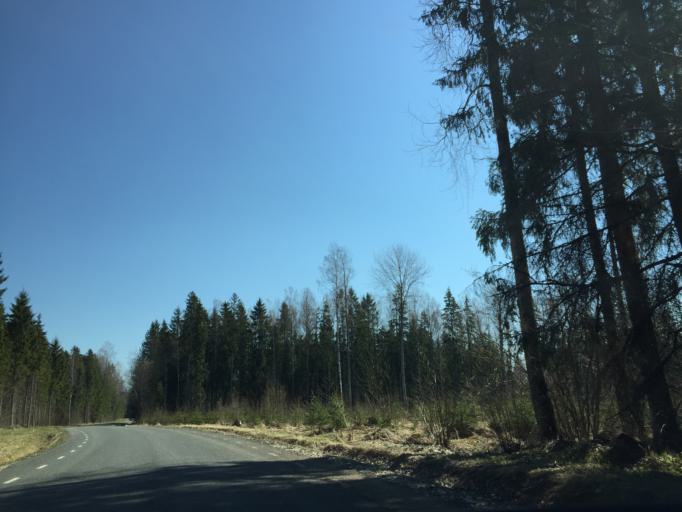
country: EE
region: Tartu
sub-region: Alatskivi vald
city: Kallaste
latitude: 58.5764
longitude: 26.9352
